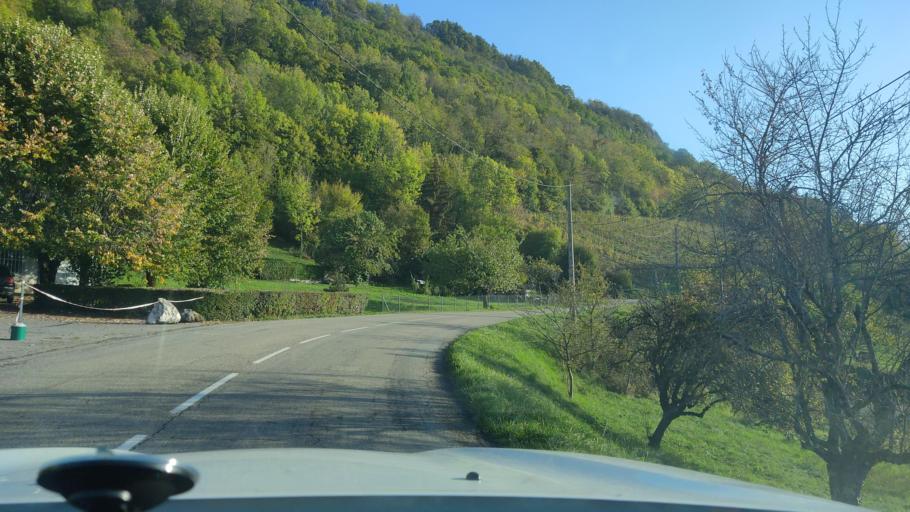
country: FR
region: Rhone-Alpes
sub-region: Departement de la Savoie
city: Coise-Saint-Jean-Pied-Gauthier
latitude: 45.5731
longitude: 6.1626
